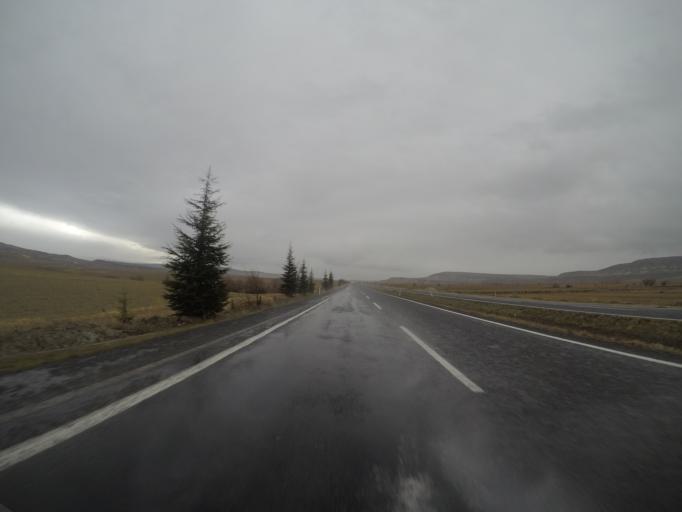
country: TR
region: Nevsehir
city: Urgub
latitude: 38.7221
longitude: 34.9491
